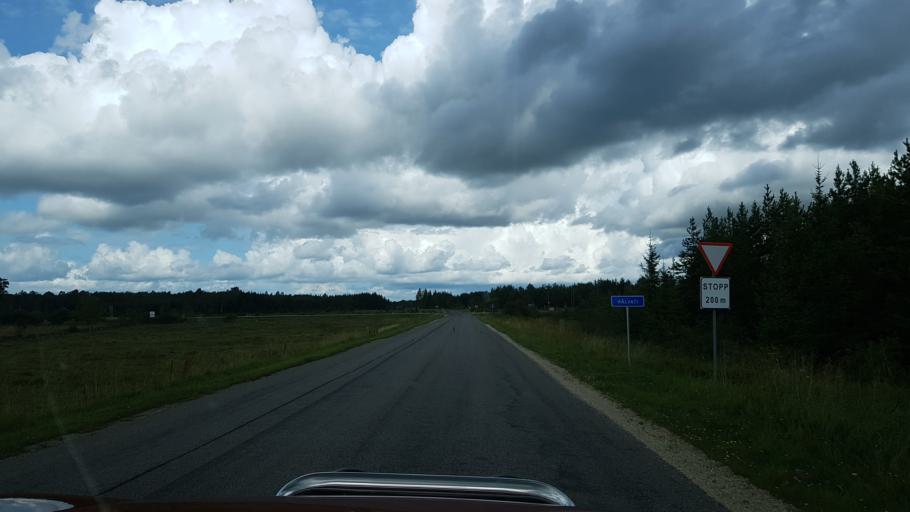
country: EE
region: Laeaene
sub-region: Lihula vald
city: Lihula
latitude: 58.6959
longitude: 23.8297
